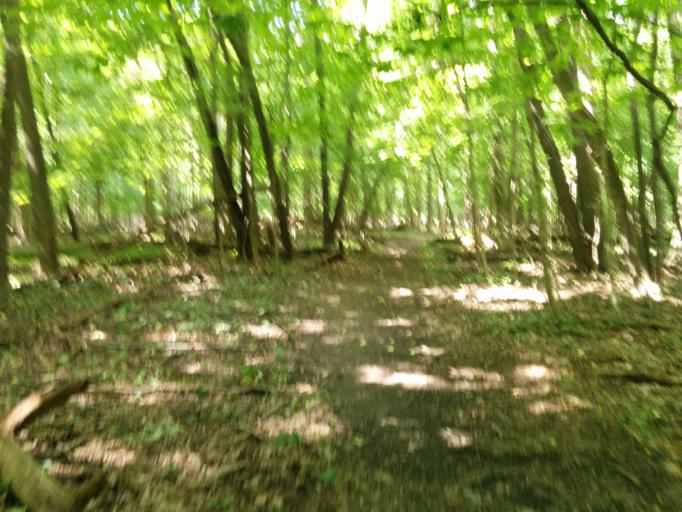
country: US
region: Illinois
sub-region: Lake County
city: Riverwoods
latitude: 42.1503
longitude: -87.9040
